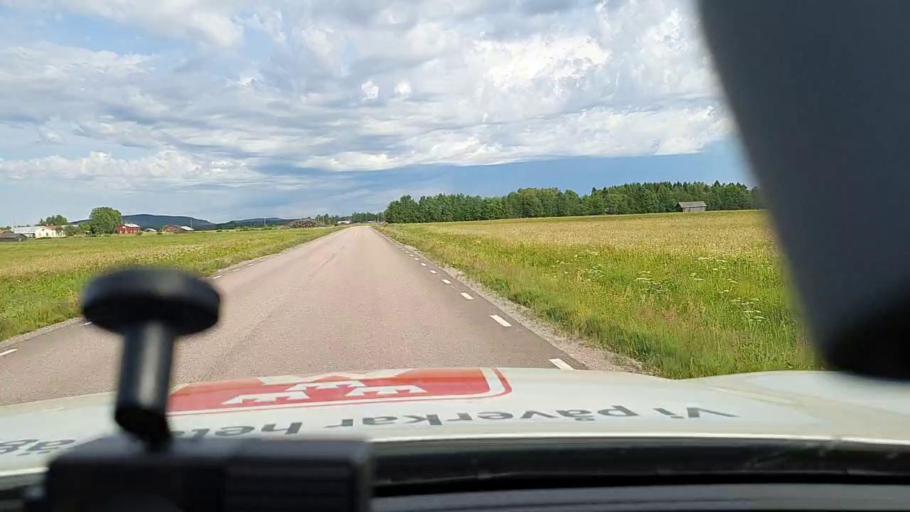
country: SE
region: Norrbotten
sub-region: Bodens Kommun
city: Saevast
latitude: 65.6976
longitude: 21.7757
